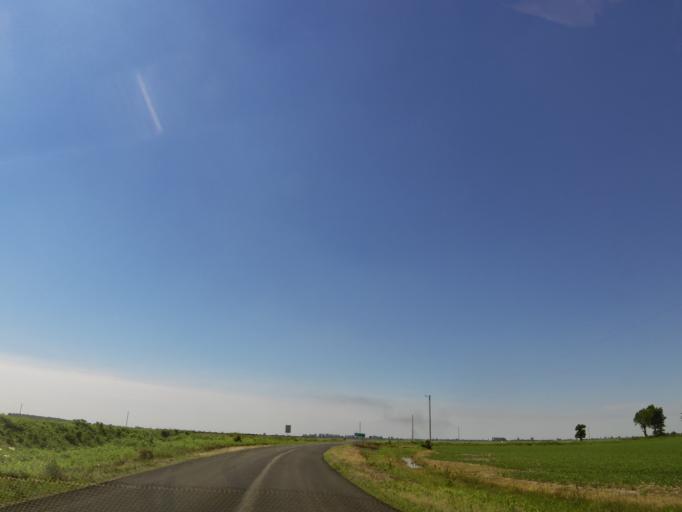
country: US
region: Missouri
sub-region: New Madrid County
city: Lilbourn
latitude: 36.5563
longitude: -89.7031
